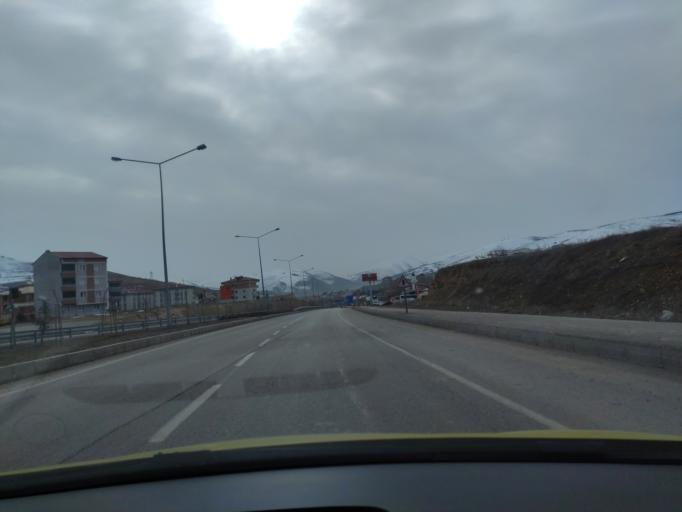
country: TR
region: Bayburt
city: Bayburt
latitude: 40.2644
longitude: 40.2052
